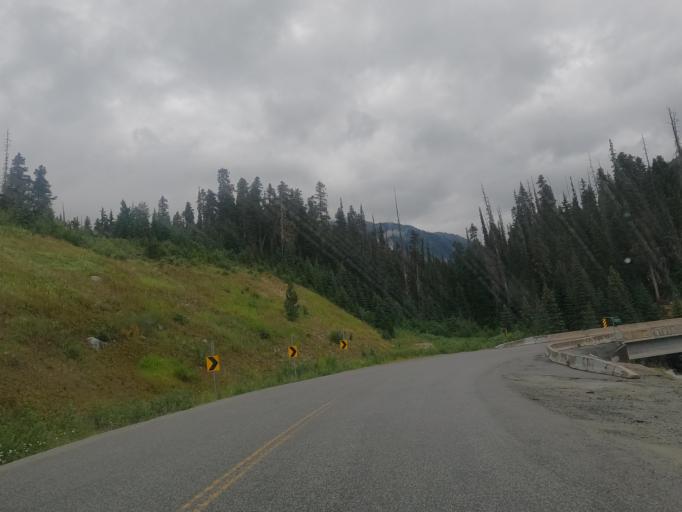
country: CA
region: British Columbia
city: Pemberton
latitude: 50.3842
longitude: -122.4697
